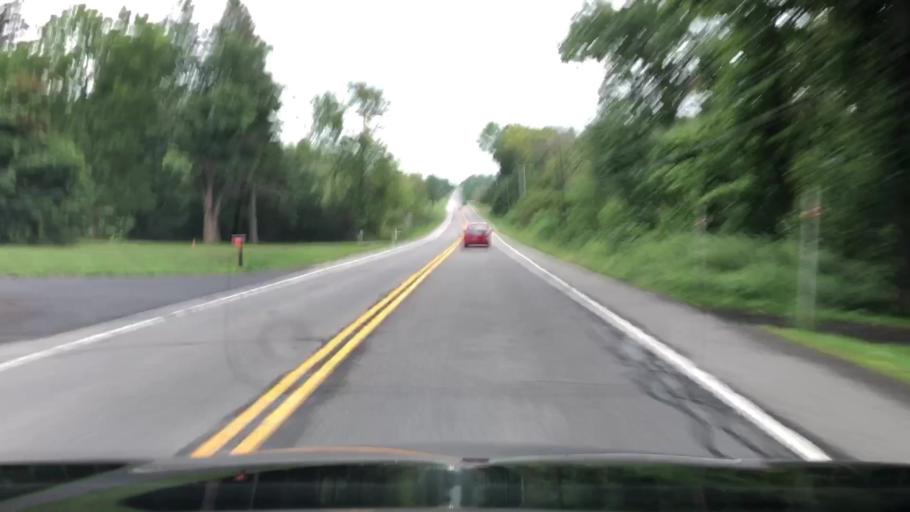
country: US
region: New York
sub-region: Erie County
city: Orchard Park
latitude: 42.7809
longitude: -78.6970
